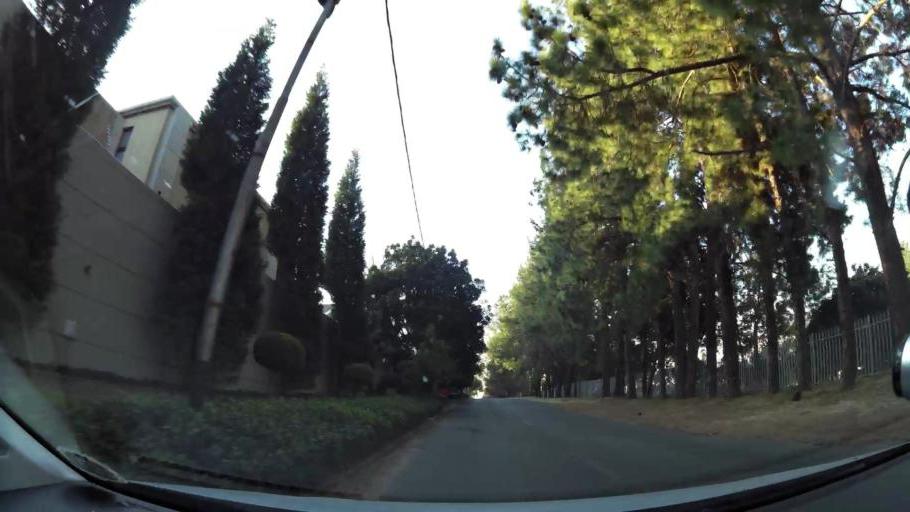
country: ZA
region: Gauteng
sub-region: City of Johannesburg Metropolitan Municipality
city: Johannesburg
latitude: -26.1594
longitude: 28.0556
